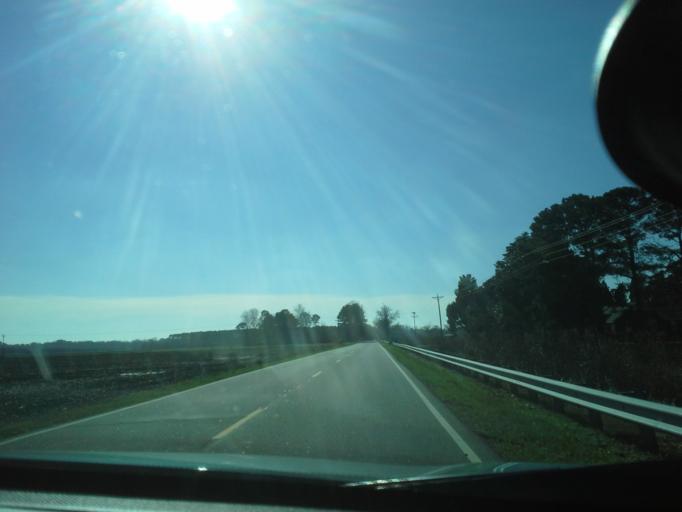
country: US
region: North Carolina
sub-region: Beaufort County
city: Belhaven
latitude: 35.6077
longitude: -76.6573
